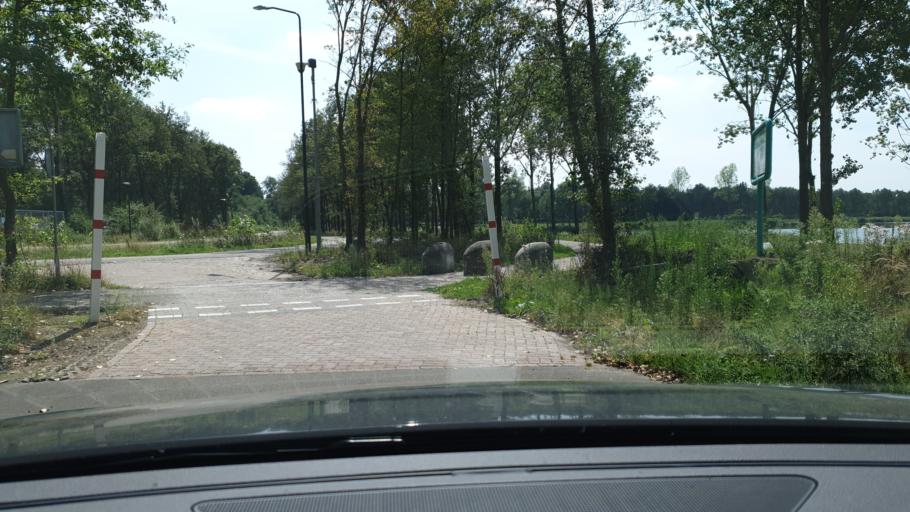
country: NL
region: North Brabant
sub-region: Gemeente Son en Breugel
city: Son
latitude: 51.4984
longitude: 5.4505
